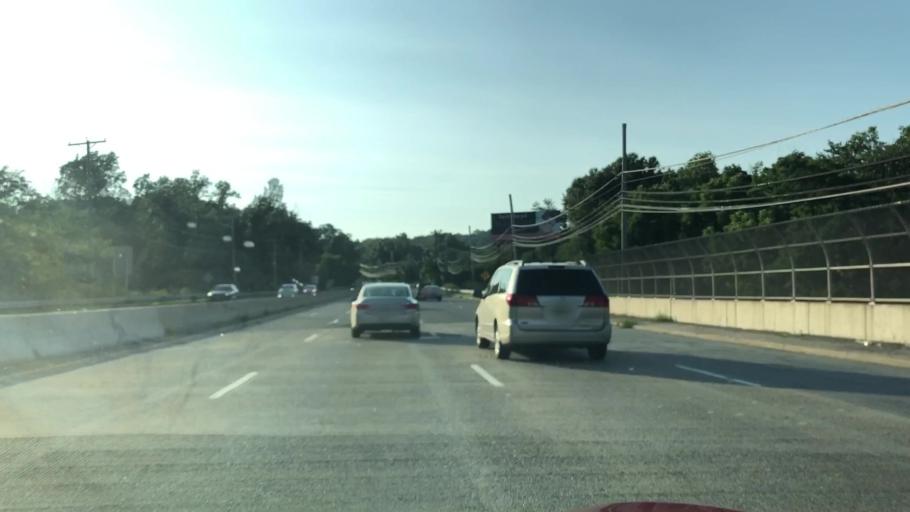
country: US
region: New Jersey
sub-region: Morris County
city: Morris Plains
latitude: 40.8518
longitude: -74.4744
